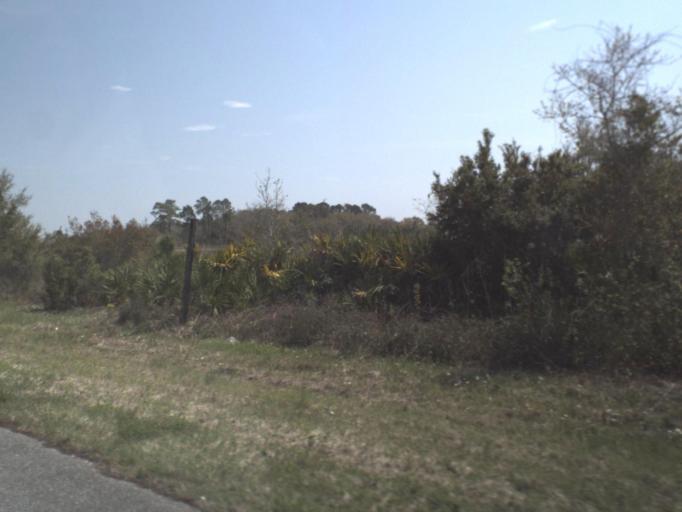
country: US
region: Florida
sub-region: Franklin County
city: Apalachicola
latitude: 29.7230
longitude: -85.0743
